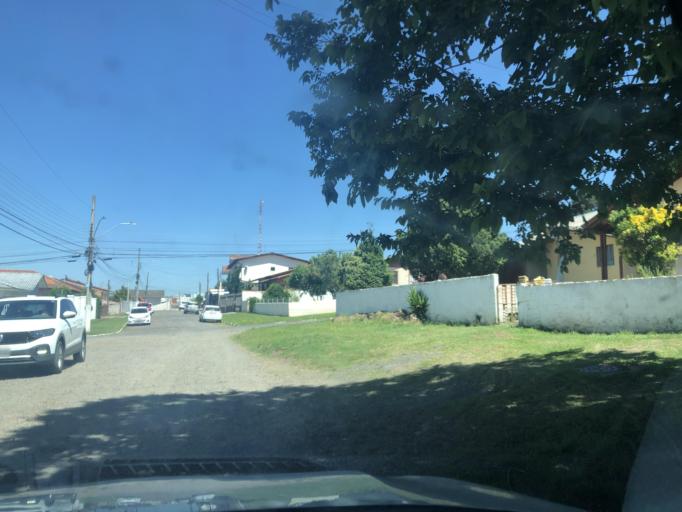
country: BR
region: Santa Catarina
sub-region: Lages
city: Lages
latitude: -27.8217
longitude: -50.3083
